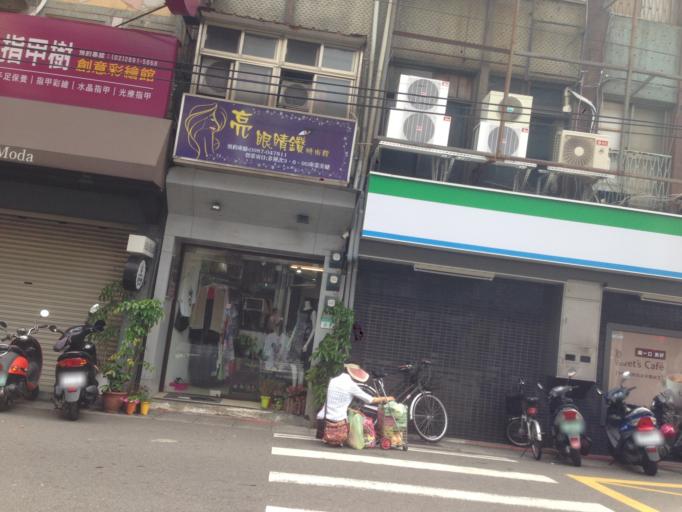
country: TW
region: Taipei
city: Taipei
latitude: 25.1319
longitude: 121.5015
